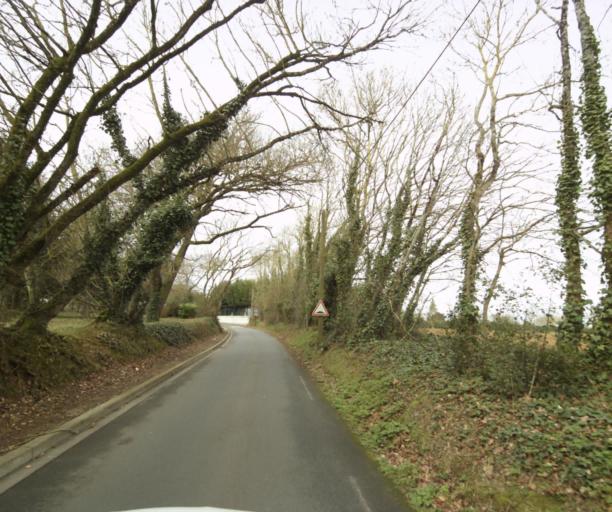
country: FR
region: Poitou-Charentes
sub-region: Departement de la Charente-Maritime
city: Lagord
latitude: 46.1892
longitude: -1.1650
